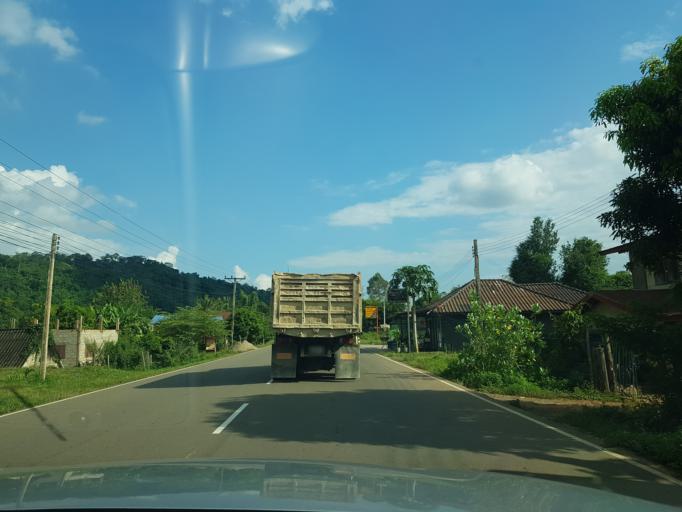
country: TH
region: Nong Khai
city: Sangkhom
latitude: 18.0154
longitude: 102.3971
